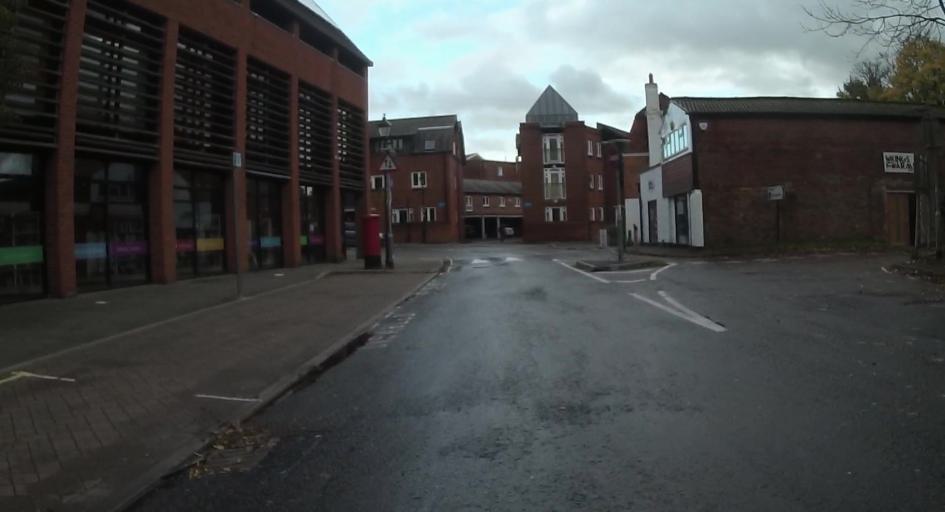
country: GB
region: England
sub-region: Hampshire
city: Alton
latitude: 51.1497
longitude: -0.9764
